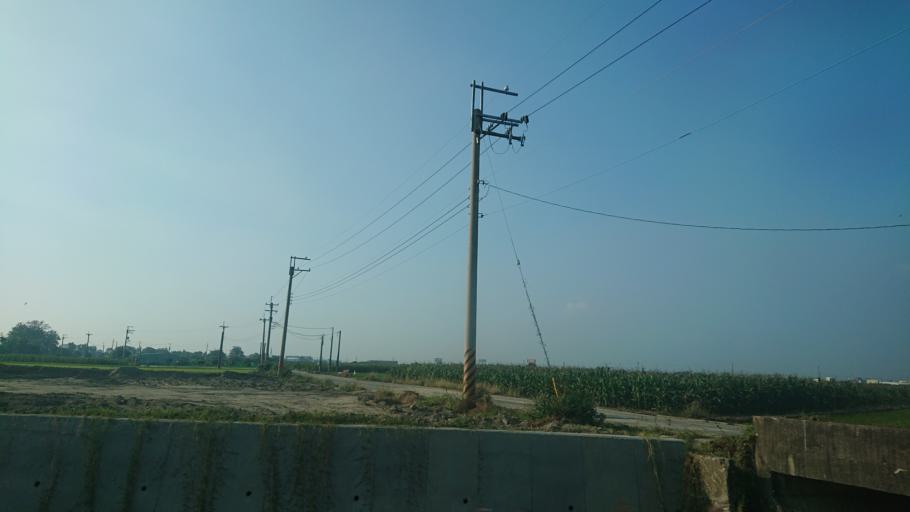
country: TW
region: Taiwan
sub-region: Tainan
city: Tainan
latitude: 23.1369
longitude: 120.2399
